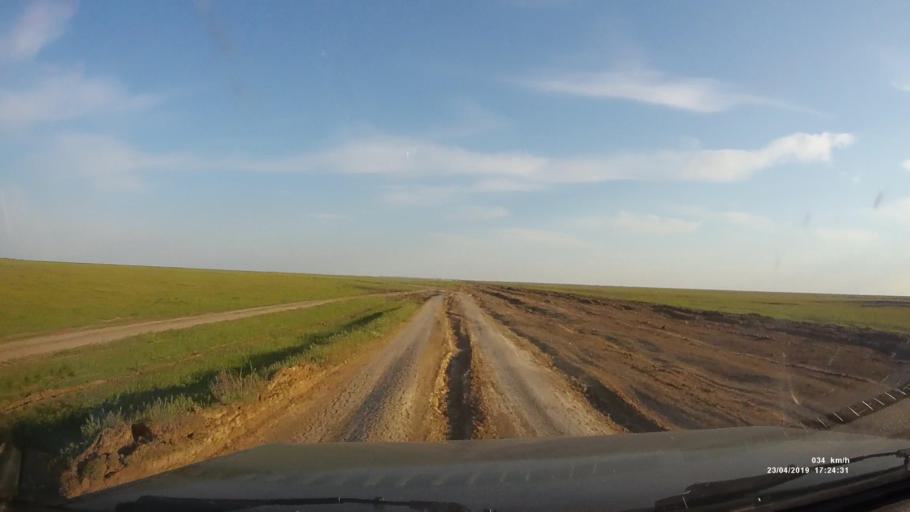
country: RU
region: Kalmykiya
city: Priyutnoye
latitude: 46.1567
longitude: 43.5087
